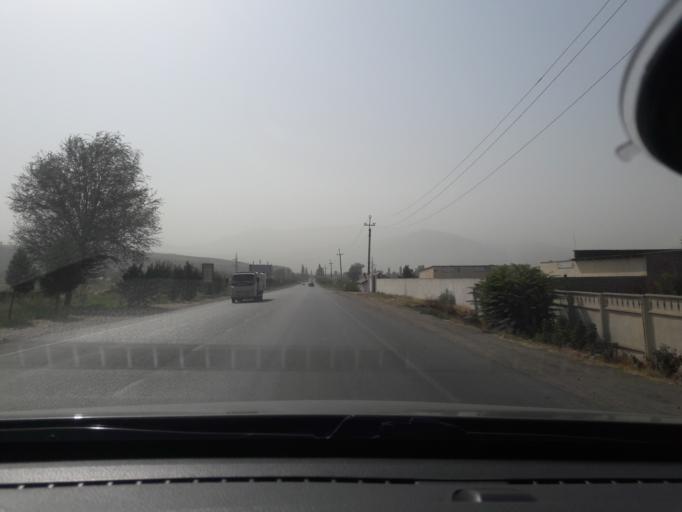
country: TJ
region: Republican Subordination
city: Vahdat
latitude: 38.5303
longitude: 69.0259
